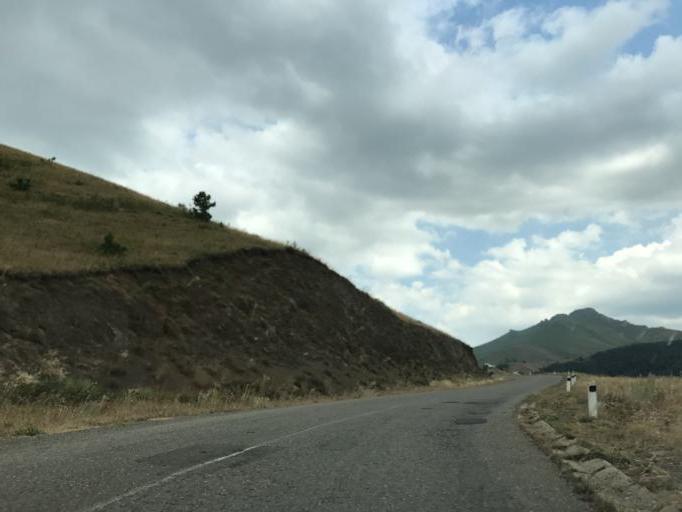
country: AZ
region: Susa
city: Shushi
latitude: 39.6921
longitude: 46.6431
